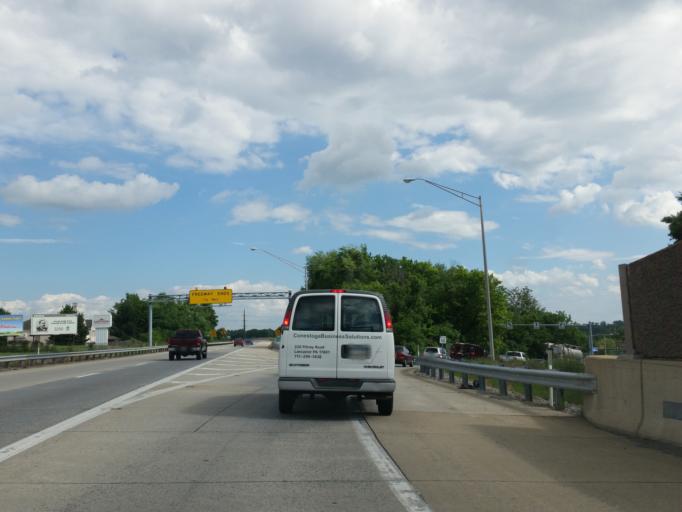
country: US
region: Pennsylvania
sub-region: Lancaster County
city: Lampeter
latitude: 40.0347
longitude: -76.2427
